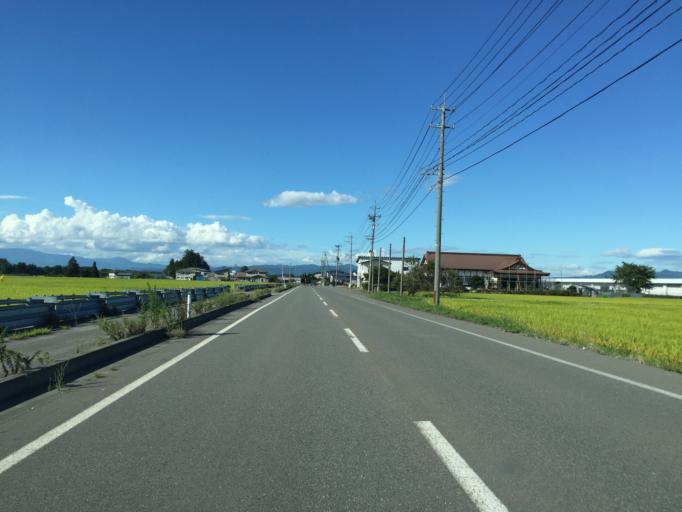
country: JP
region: Yamagata
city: Yonezawa
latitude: 37.9505
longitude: 140.1081
